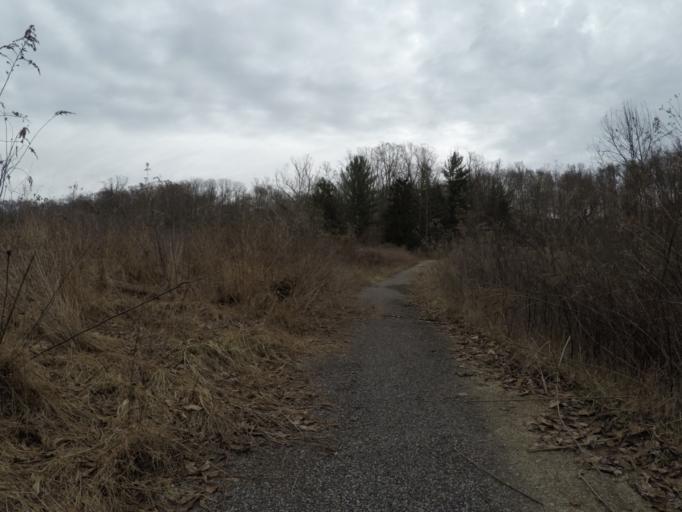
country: US
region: Ohio
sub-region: Lawrence County
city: Burlington
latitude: 38.3819
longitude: -82.5091
